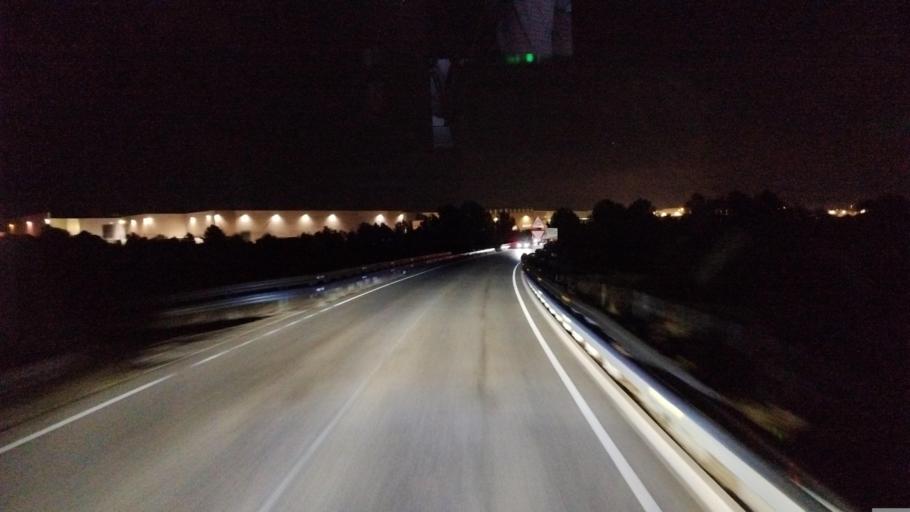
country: ES
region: Catalonia
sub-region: Provincia de Tarragona
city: la Bisbal del Penedes
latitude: 41.2683
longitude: 1.5023
